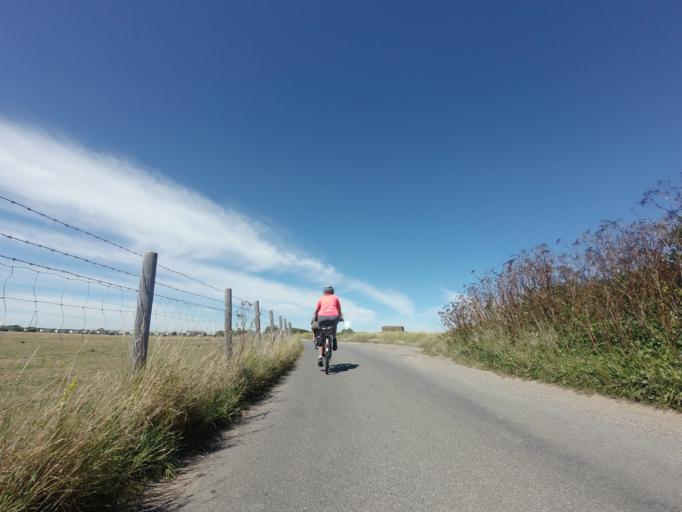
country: GB
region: England
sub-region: Kent
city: Deal
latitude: 51.2473
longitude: 1.3949
